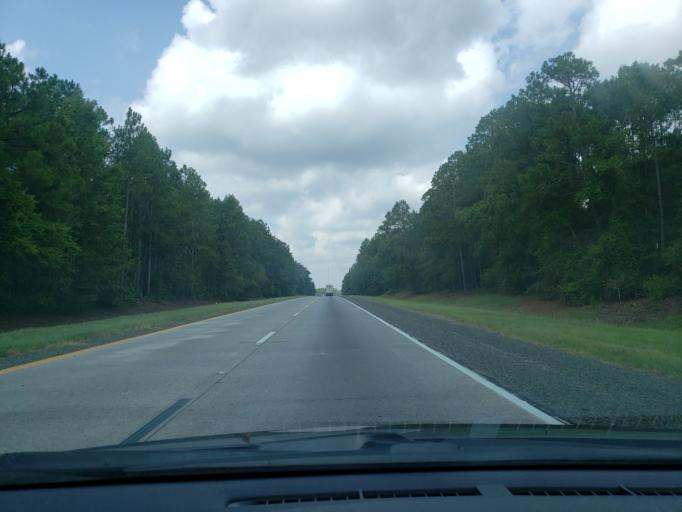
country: US
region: Georgia
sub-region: Treutlen County
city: Soperton
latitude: 32.4349
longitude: -82.6419
